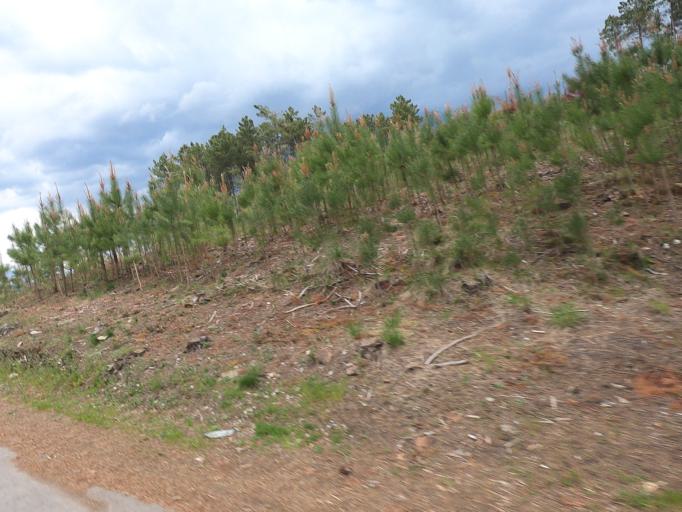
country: PT
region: Vila Real
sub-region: Sabrosa
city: Vilela
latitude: 41.2503
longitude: -7.6577
